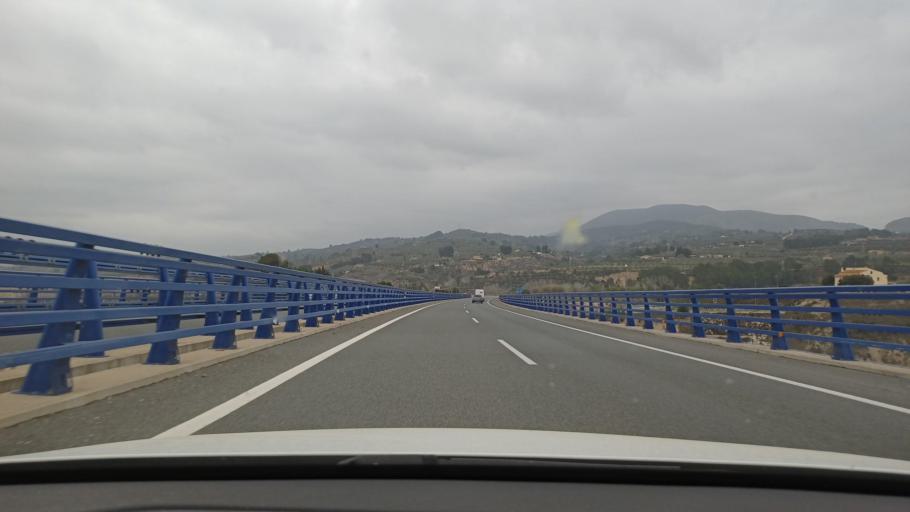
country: ES
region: Valencia
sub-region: Provincia de Alicante
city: Cocentaina
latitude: 38.7354
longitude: -0.4300
